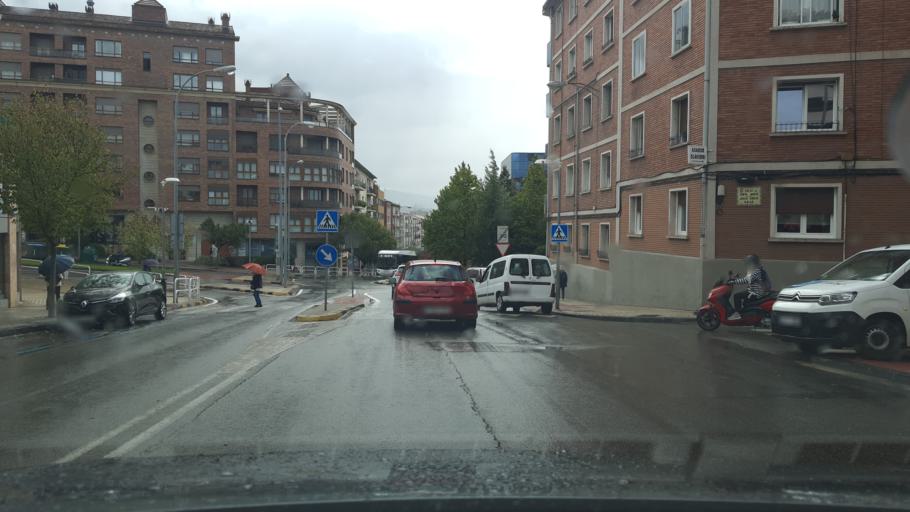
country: ES
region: Navarre
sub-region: Provincia de Navarra
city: Segundo Ensanche
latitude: 42.8073
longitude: -1.6358
